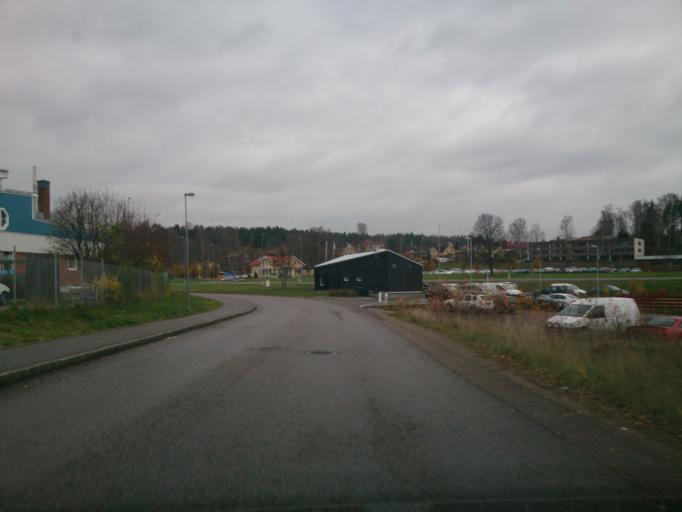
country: SE
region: OEstergoetland
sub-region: Atvidabergs Kommun
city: Atvidaberg
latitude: 58.2012
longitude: 16.0030
